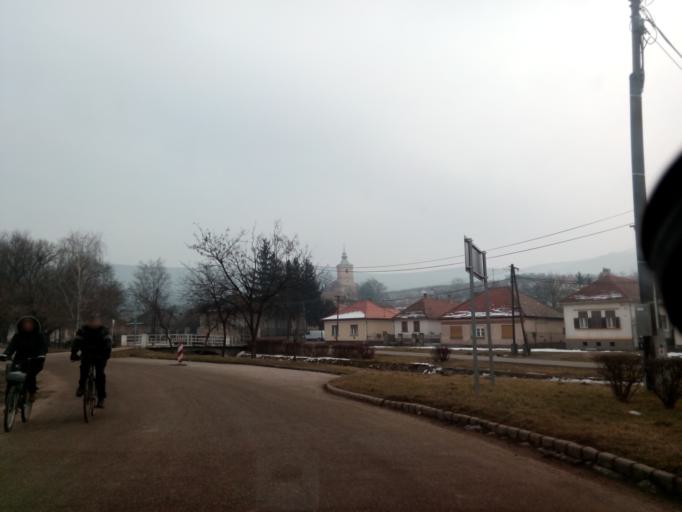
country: HU
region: Borsod-Abauj-Zemplen
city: Gonc
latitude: 48.4713
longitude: 21.2739
